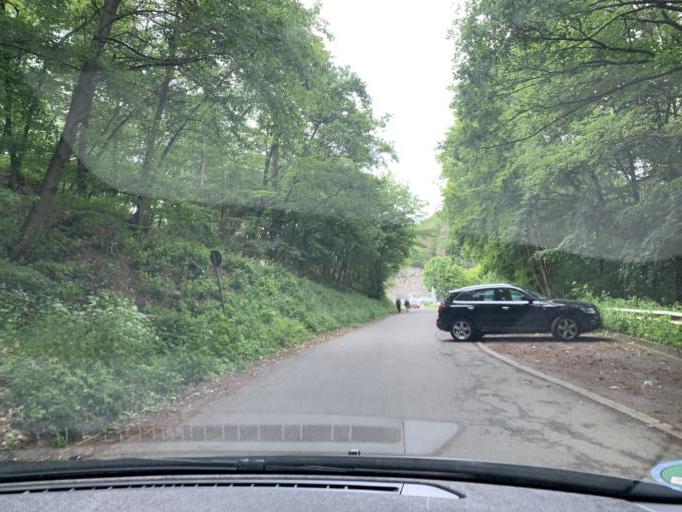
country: DE
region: North Rhine-Westphalia
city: Heimbach
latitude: 50.6454
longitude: 6.4138
